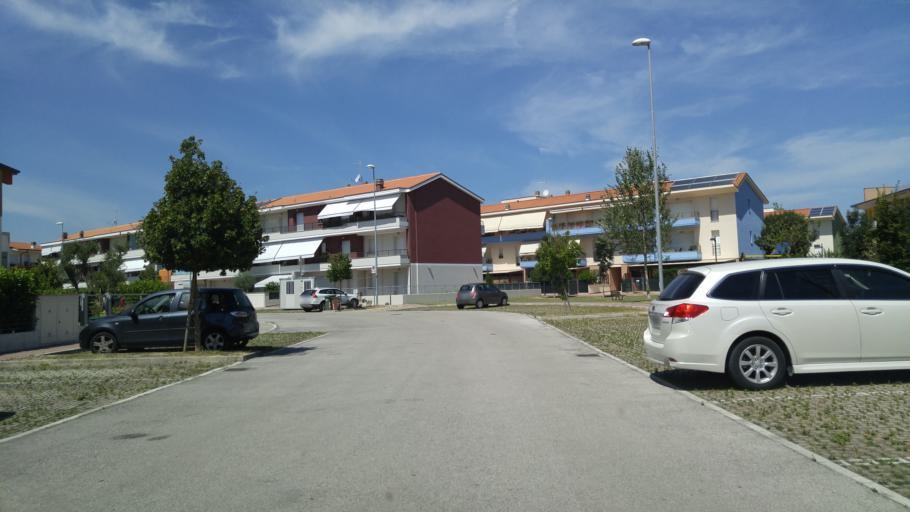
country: IT
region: The Marches
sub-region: Provincia di Pesaro e Urbino
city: Rosciano
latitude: 43.8042
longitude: 12.9940
